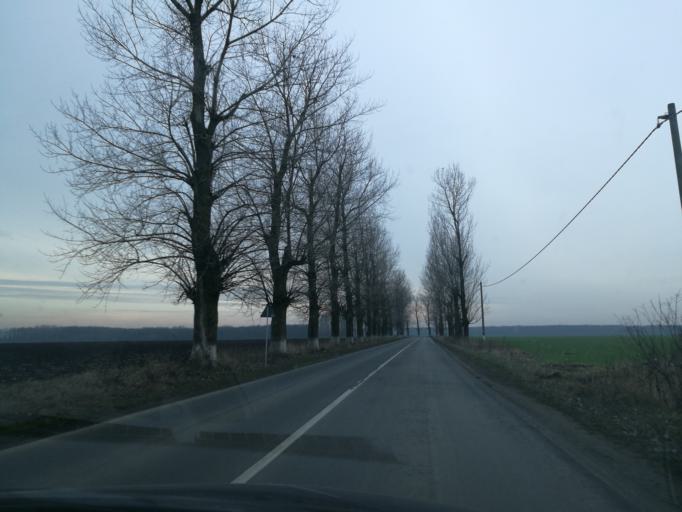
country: RO
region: Ilfov
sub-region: Comuna Gradistea
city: Gradistea
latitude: 44.6501
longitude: 26.3044
